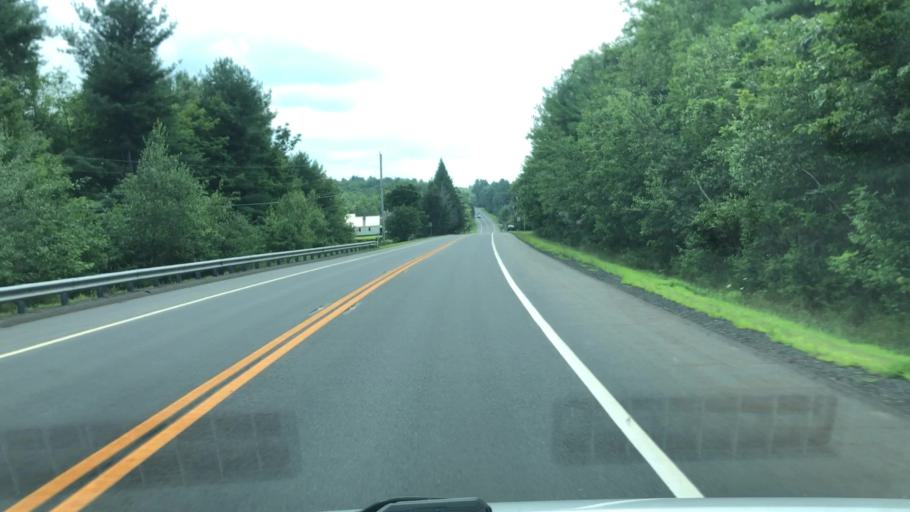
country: US
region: Massachusetts
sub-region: Franklin County
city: Ashfield
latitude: 42.4953
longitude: -72.8077
